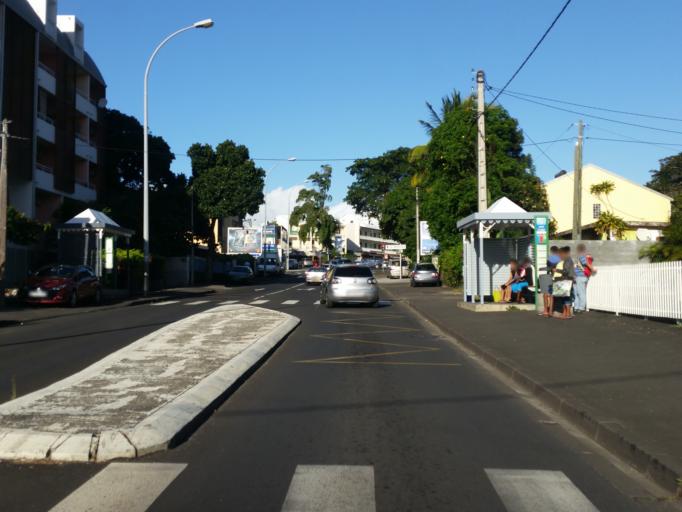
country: RE
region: Reunion
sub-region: Reunion
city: Saint-Denis
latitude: -20.8960
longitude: 55.4910
